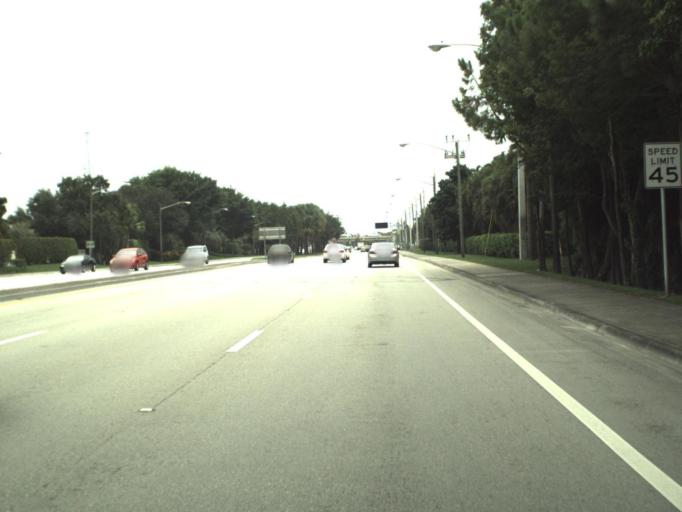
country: US
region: Florida
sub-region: Palm Beach County
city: Boca Del Mar
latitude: 26.3678
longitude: -80.1781
